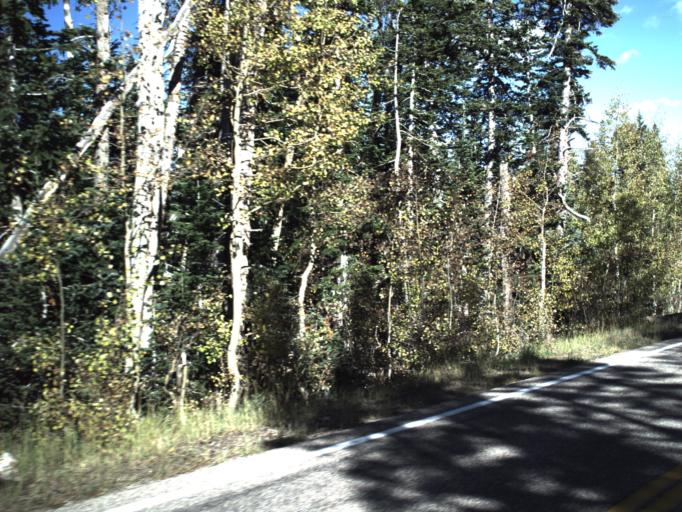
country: US
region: Utah
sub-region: Iron County
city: Parowan
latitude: 37.6541
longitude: -112.8079
